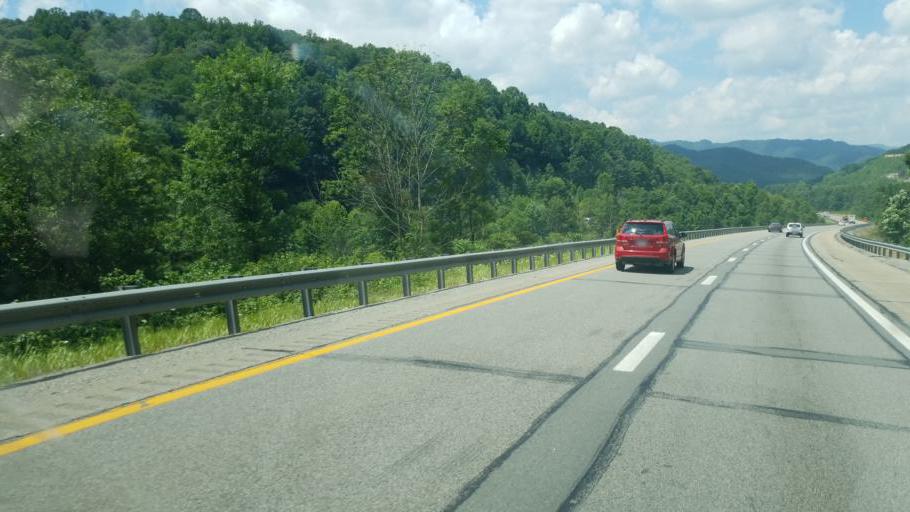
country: US
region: West Virginia
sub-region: Raleigh County
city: Prosperity
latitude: 37.8521
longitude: -81.2508
